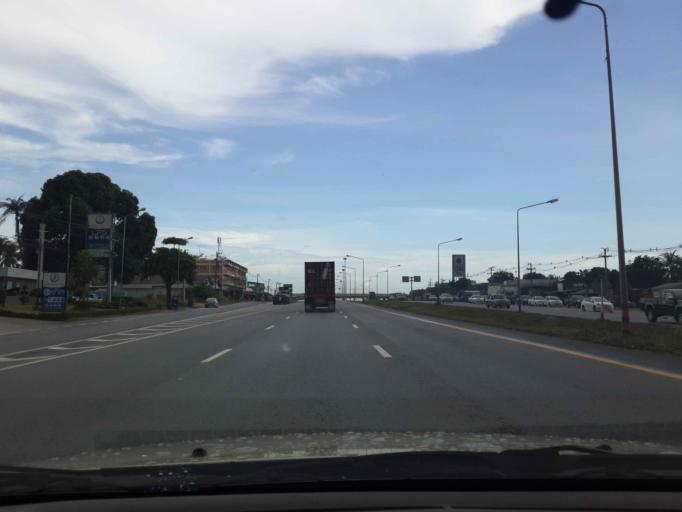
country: TH
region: Chon Buri
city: Phatthaya
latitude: 12.9491
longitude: 100.9903
